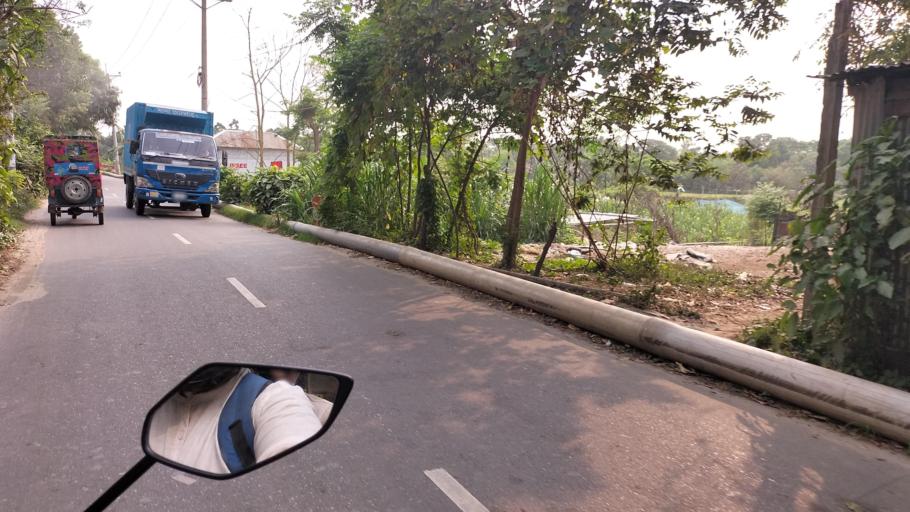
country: BD
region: Dhaka
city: Azimpur
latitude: 23.6686
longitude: 90.3418
